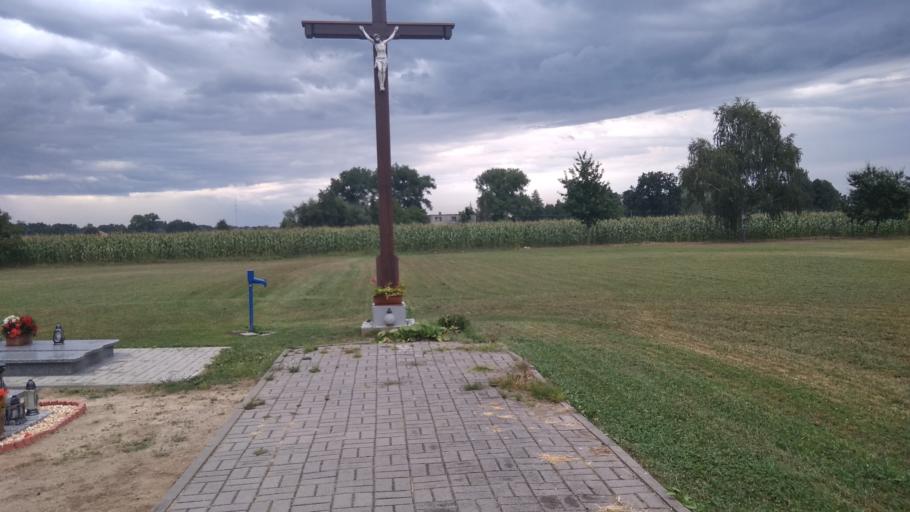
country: PL
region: Kujawsko-Pomorskie
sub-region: Powiat bydgoski
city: Osielsko
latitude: 53.2215
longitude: 18.1323
